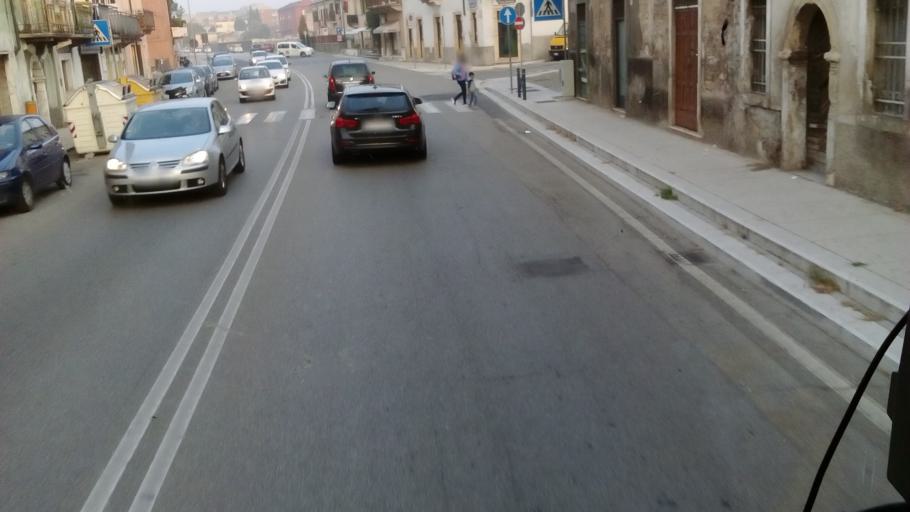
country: IT
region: Veneto
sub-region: Provincia di Verona
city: Montorio
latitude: 45.4344
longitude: 11.0403
